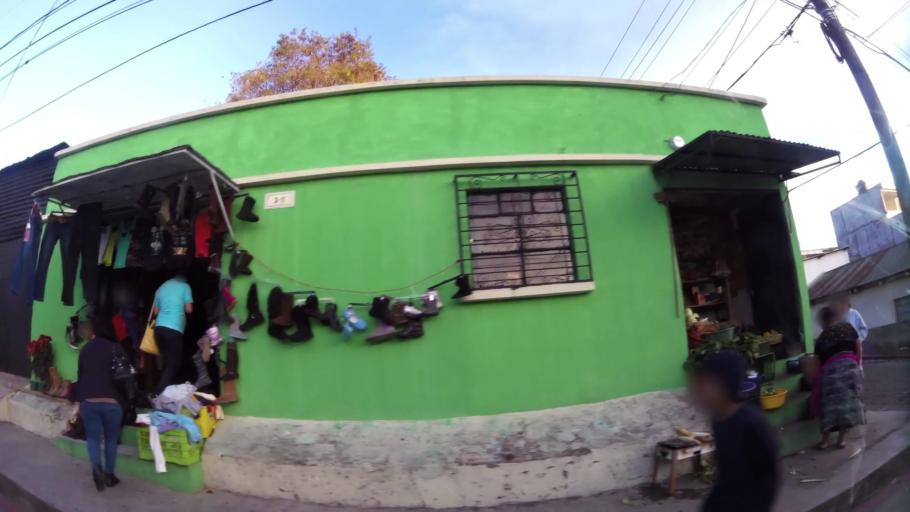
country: GT
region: Sacatepequez
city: San Lucas Sacatepequez
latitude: 14.6115
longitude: -90.6557
